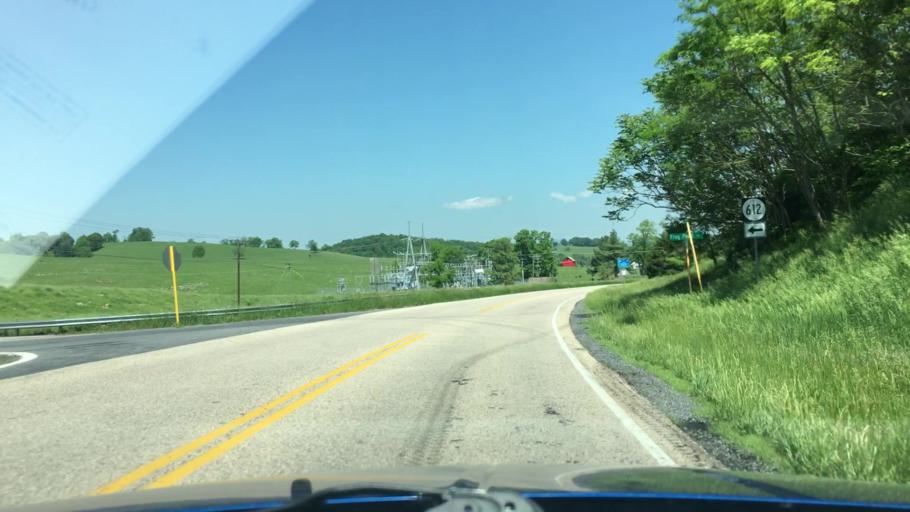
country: US
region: Virginia
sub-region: City of Staunton
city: Staunton
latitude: 38.1921
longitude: -79.1116
